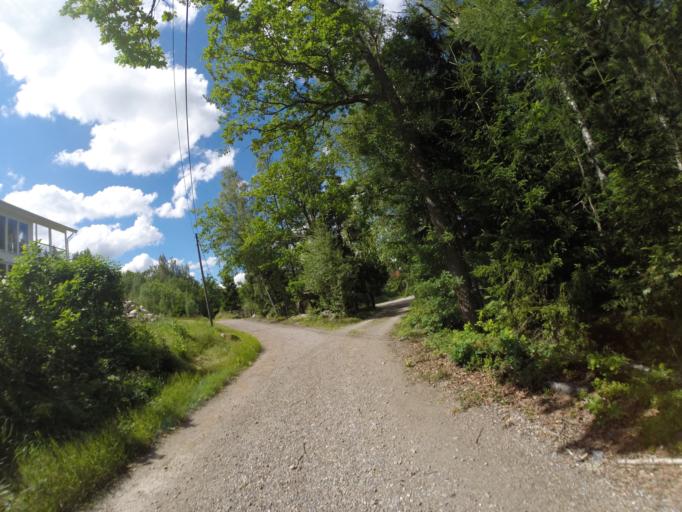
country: SE
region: Soedermanland
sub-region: Eskilstuna Kommun
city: Kvicksund
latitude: 59.4528
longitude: 16.3486
